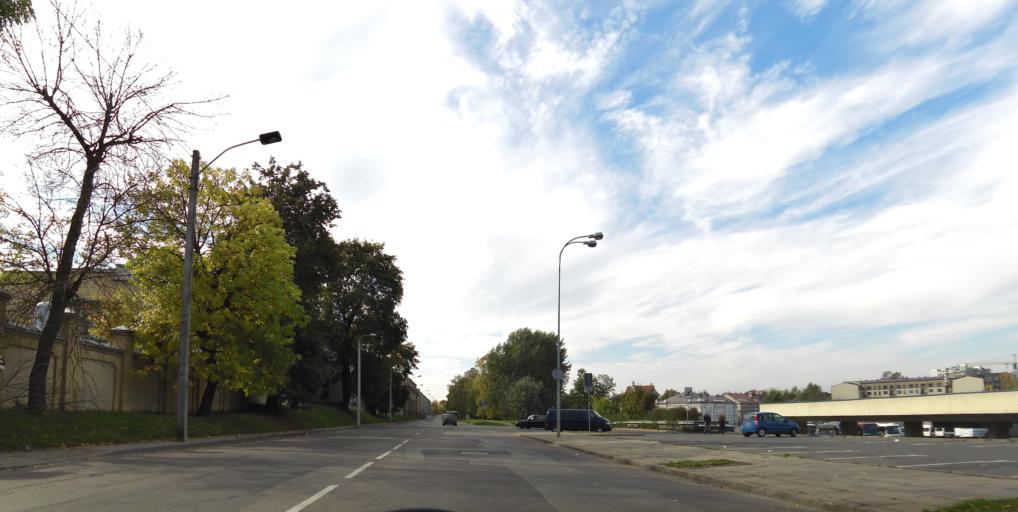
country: LT
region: Vilnius County
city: Naujamiestis
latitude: 54.6699
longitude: 25.2815
